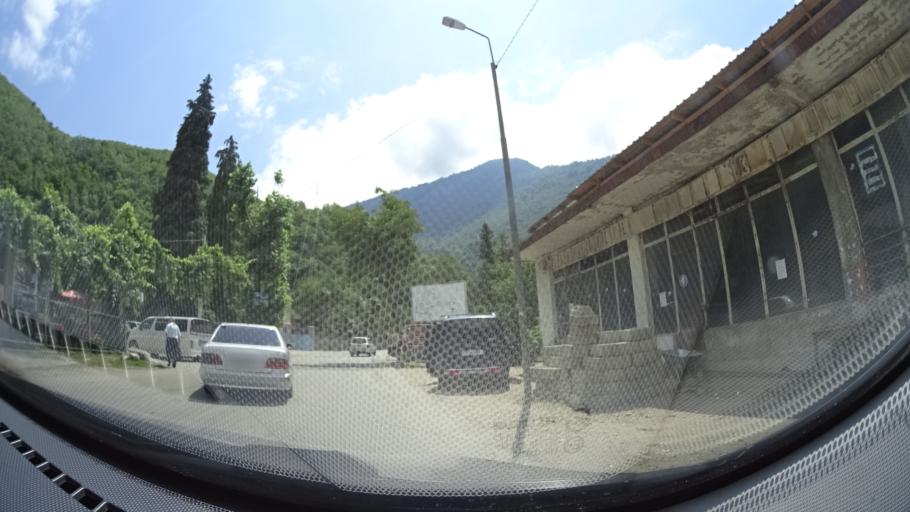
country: GE
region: Ajaria
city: Keda
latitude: 41.5719
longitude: 41.8596
